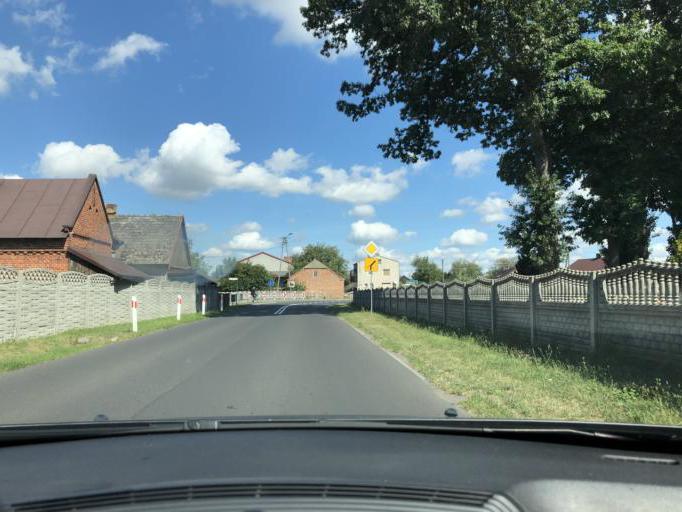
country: PL
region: Lodz Voivodeship
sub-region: Powiat wieruszowski
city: Czastary
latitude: 51.2559
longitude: 18.3169
